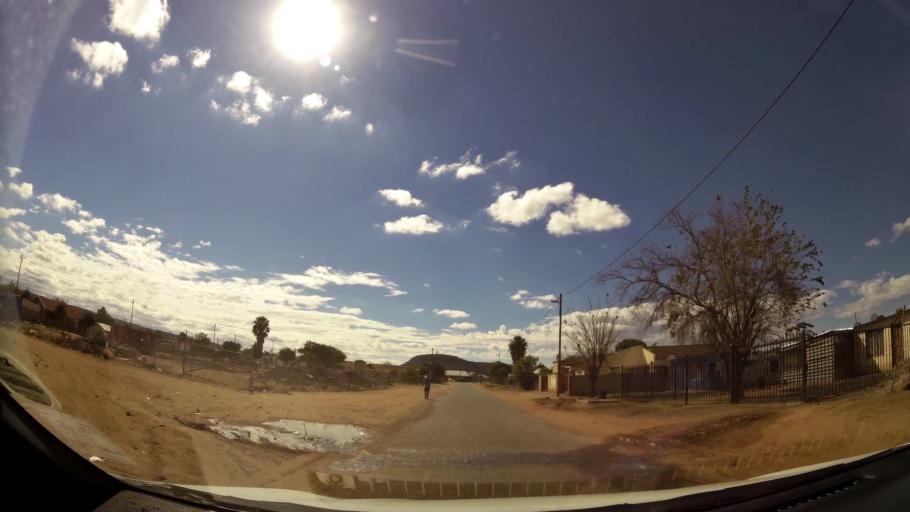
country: ZA
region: Limpopo
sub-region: Waterberg District Municipality
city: Bela-Bela
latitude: -24.8786
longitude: 28.3224
